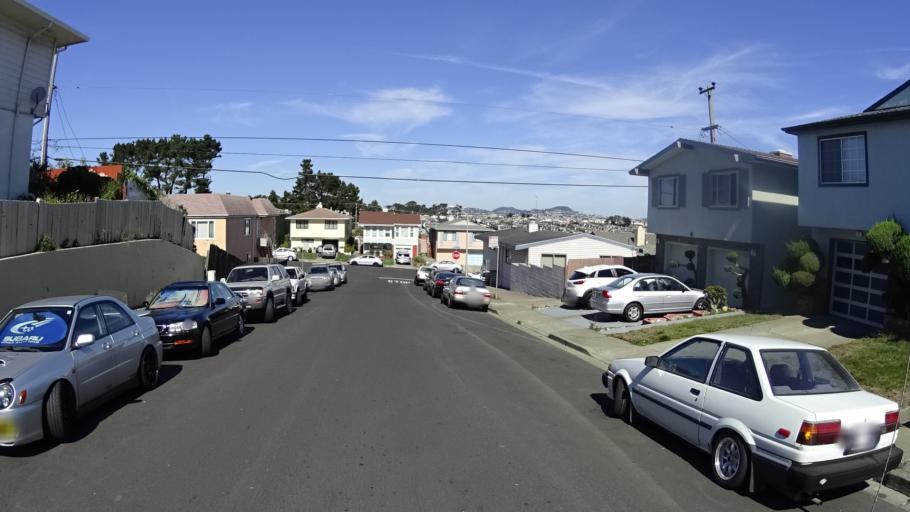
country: US
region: California
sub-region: San Mateo County
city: Broadmoor
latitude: 37.6735
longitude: -122.4811
